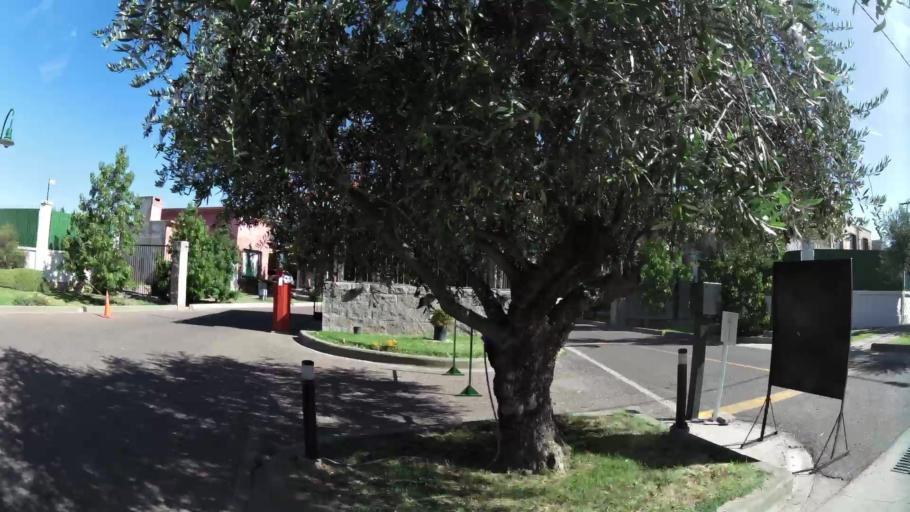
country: AR
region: Mendoza
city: Villa Nueva
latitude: -32.9106
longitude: -68.7878
